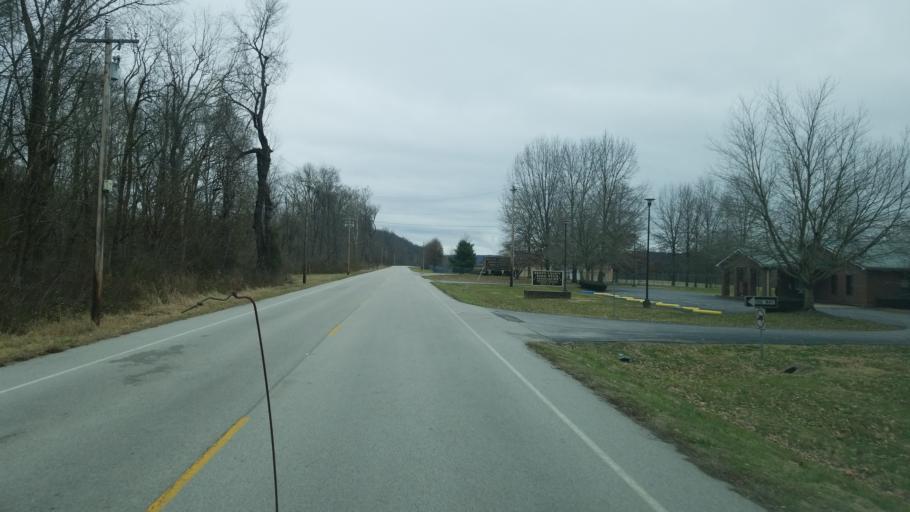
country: US
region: Kentucky
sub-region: Bracken County
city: Augusta
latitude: 38.7820
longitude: -83.9274
